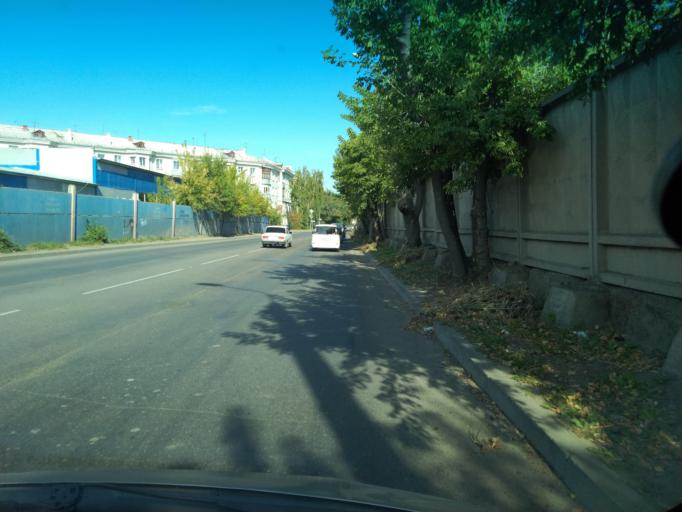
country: RU
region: Krasnoyarskiy
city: Krasnoyarsk
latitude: 56.0092
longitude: 92.9716
